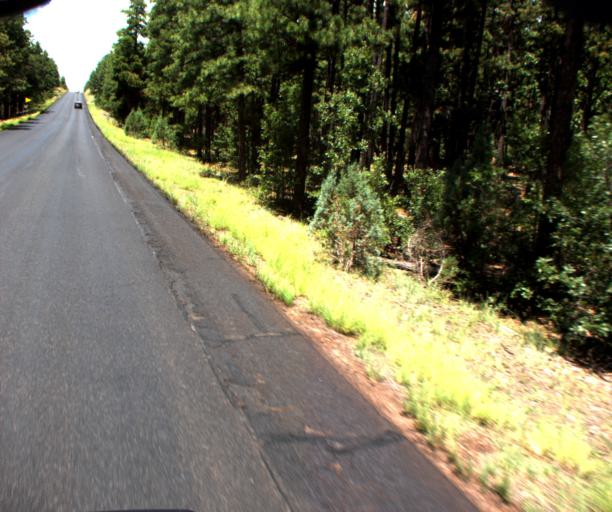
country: US
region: Arizona
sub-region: Gila County
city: Pine
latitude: 34.4824
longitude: -111.4537
